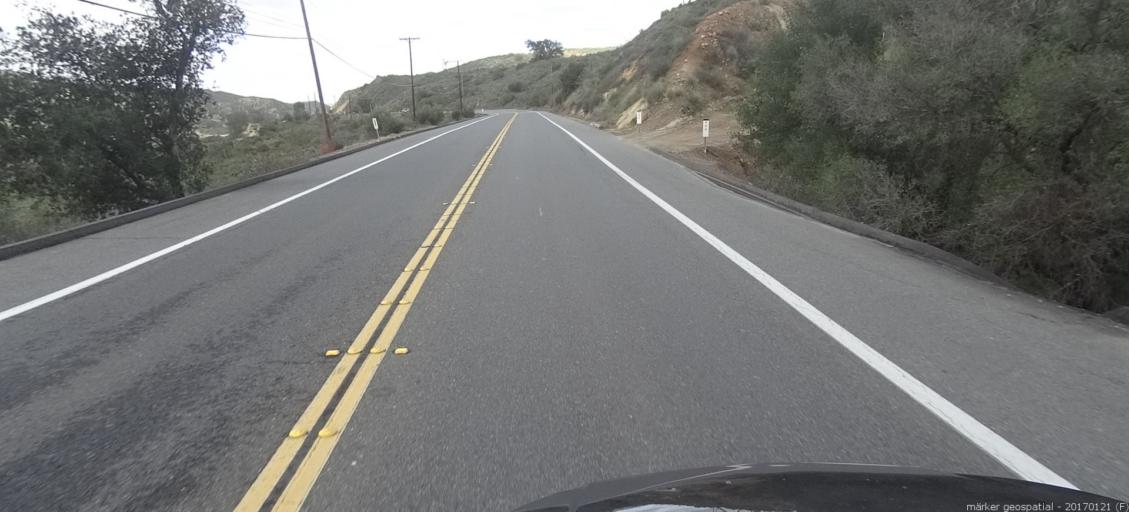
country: US
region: California
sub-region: Orange County
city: Foothill Ranch
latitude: 33.7338
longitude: -117.6532
